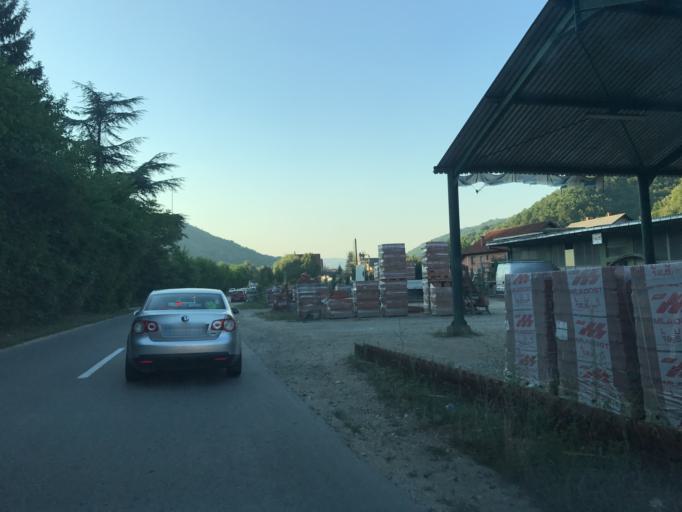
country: RO
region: Mehedinti
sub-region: Comuna Svinita
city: Svinita
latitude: 44.4260
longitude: 22.1741
